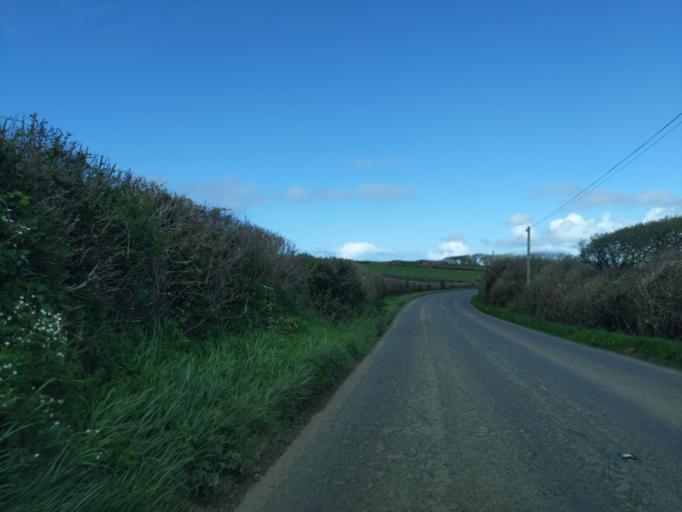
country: GB
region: England
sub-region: Cornwall
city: Tintagel
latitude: 50.5888
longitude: -4.7800
